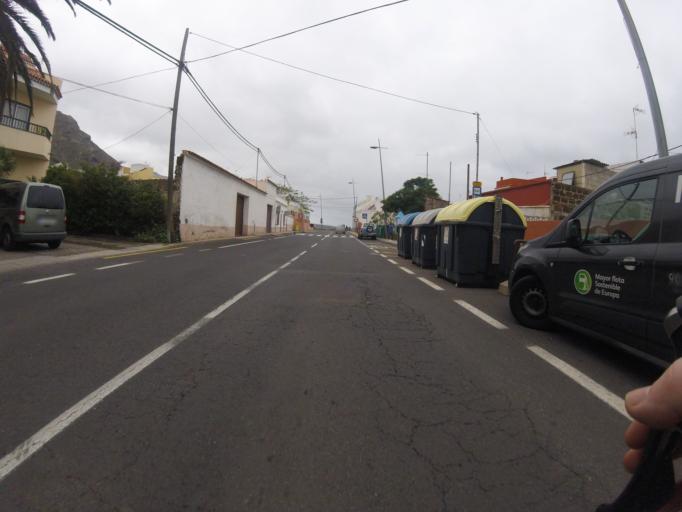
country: ES
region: Canary Islands
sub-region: Provincia de Santa Cruz de Tenerife
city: Tegueste
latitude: 28.5642
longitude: -16.3305
